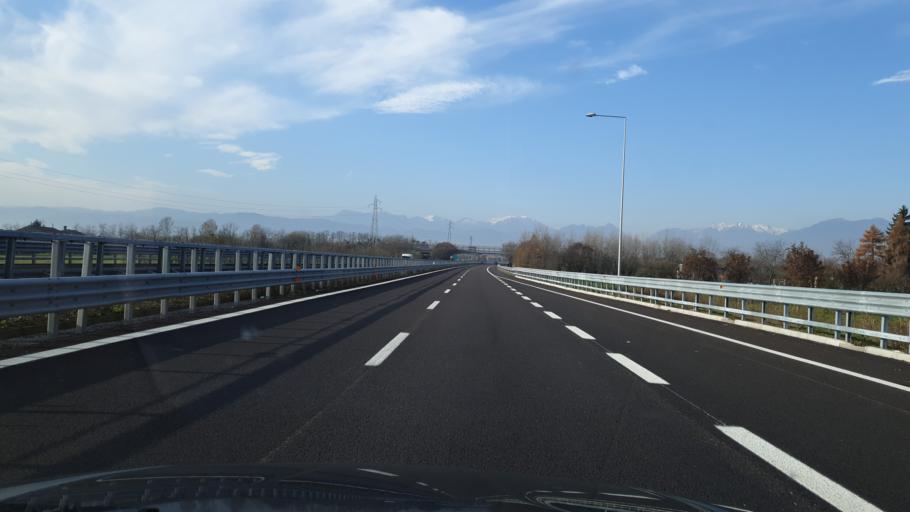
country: IT
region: Veneto
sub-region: Provincia di Vicenza
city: Novoledo
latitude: 45.6624
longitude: 11.5108
